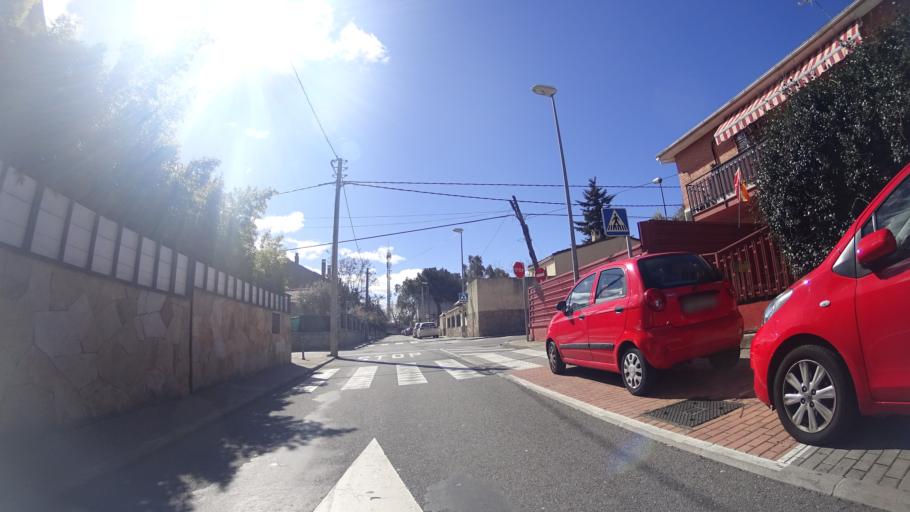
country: ES
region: Madrid
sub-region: Provincia de Madrid
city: Las Matas
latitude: 40.5540
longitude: -3.8959
